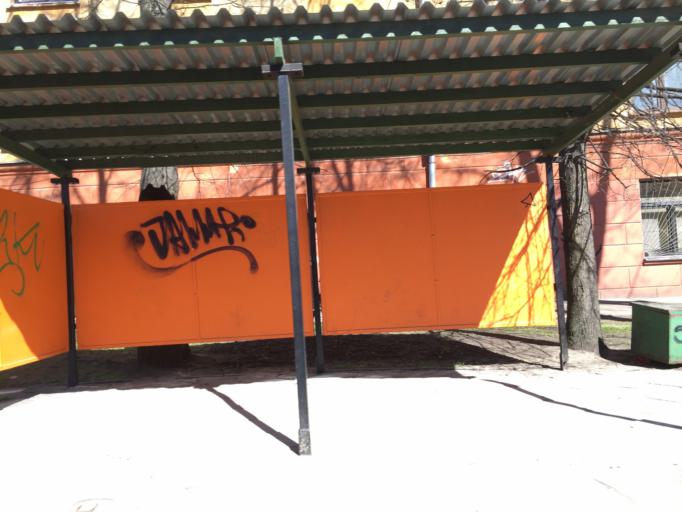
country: LV
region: Riga
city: Riga
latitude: 56.9369
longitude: 24.0771
